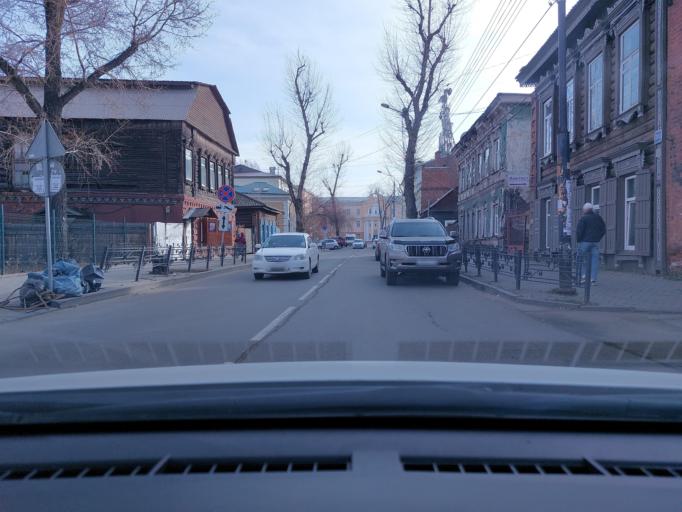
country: RU
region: Irkutsk
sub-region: Irkutskiy Rayon
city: Irkutsk
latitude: 52.2804
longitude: 104.2917
